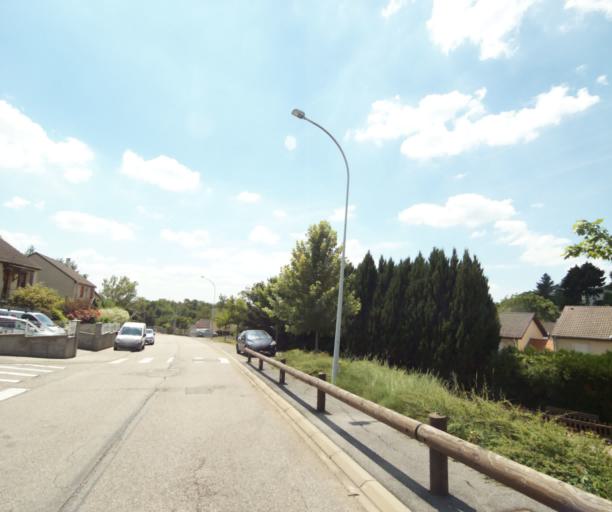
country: FR
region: Lorraine
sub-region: Departement de Meurthe-et-Moselle
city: Luneville
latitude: 48.6028
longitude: 6.4800
